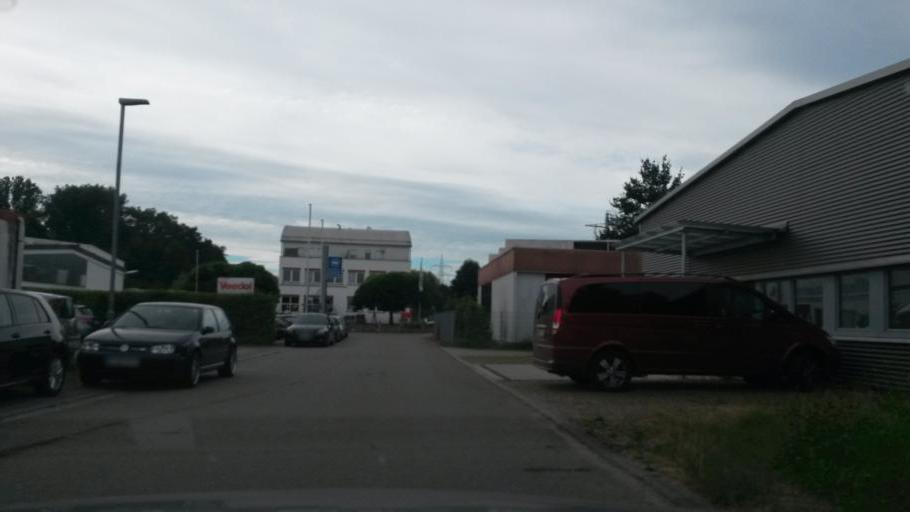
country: DE
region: Baden-Wuerttemberg
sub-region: Karlsruhe Region
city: Konigsbach-Stein
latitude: 48.9091
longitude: 8.5623
